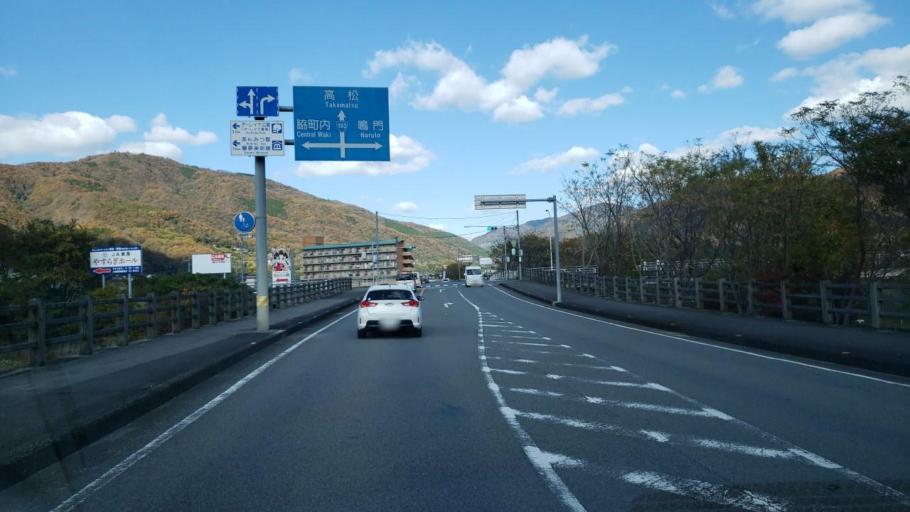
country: JP
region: Tokushima
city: Wakimachi
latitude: 34.0773
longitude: 134.1729
